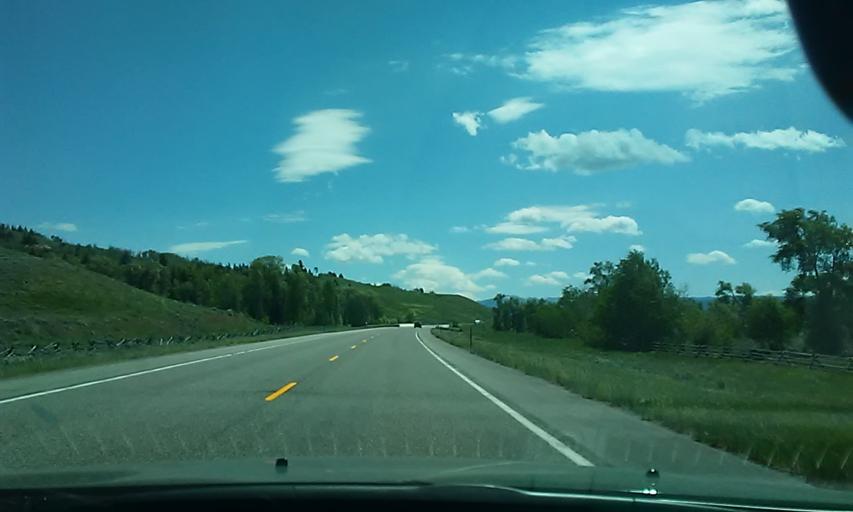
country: US
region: Wyoming
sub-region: Teton County
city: Jackson
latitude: 43.8402
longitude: -110.4608
